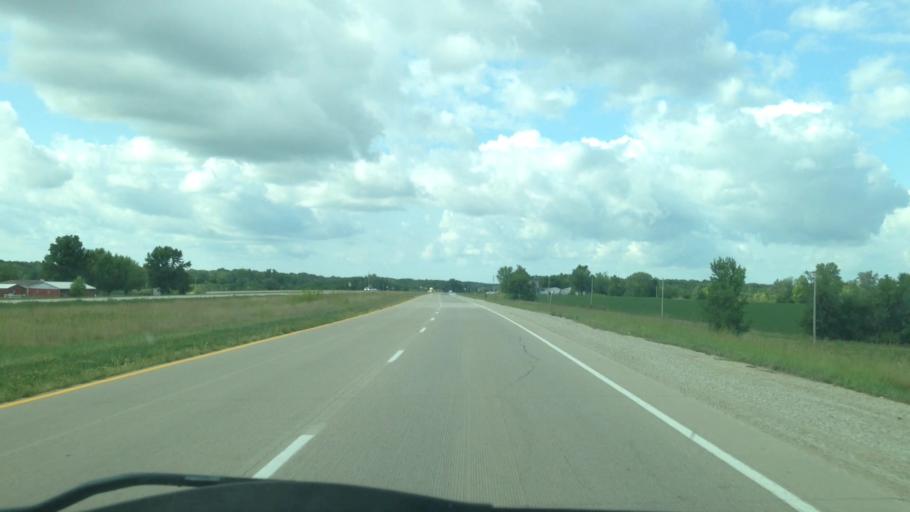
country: US
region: Illinois
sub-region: Hancock County
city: Nauvoo
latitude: 40.5377
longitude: -91.5631
